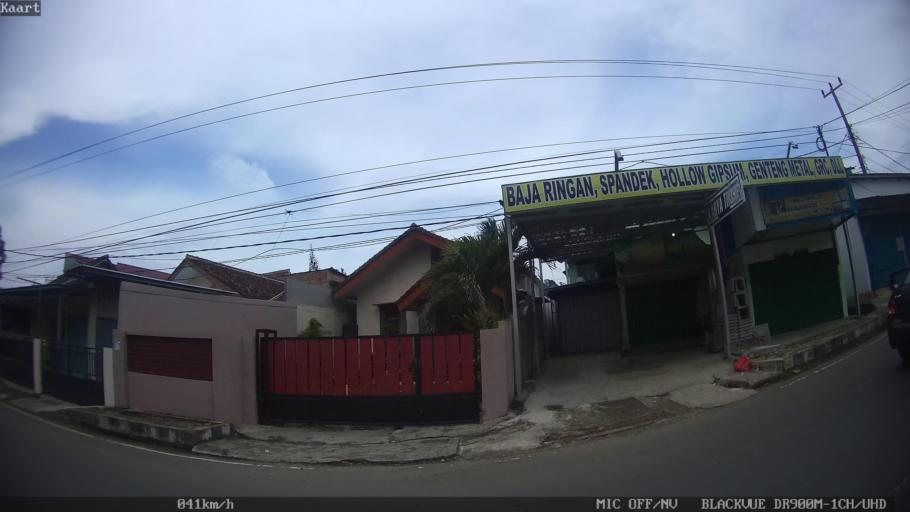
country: ID
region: Lampung
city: Kedaton
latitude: -5.3909
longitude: 105.2170
